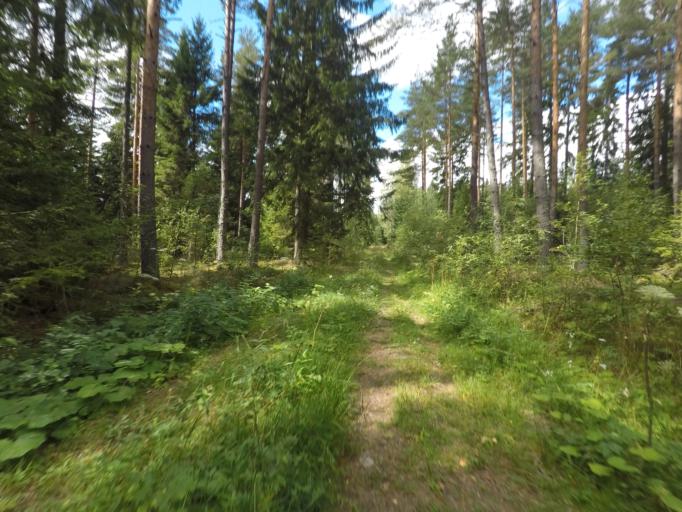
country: SE
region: Soedermanland
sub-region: Eskilstuna Kommun
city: Kvicksund
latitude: 59.4024
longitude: 16.3019
